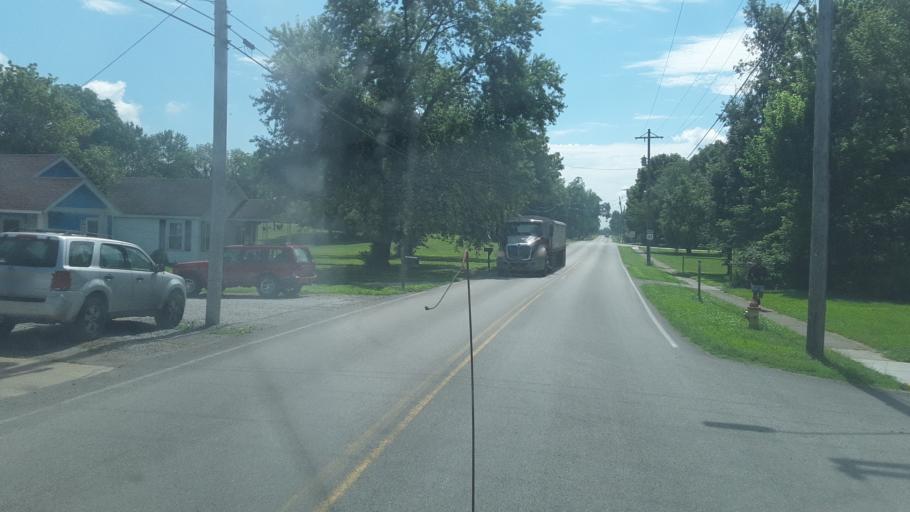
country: US
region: Kentucky
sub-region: Christian County
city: Oak Grove
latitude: 36.7782
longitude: -87.3529
